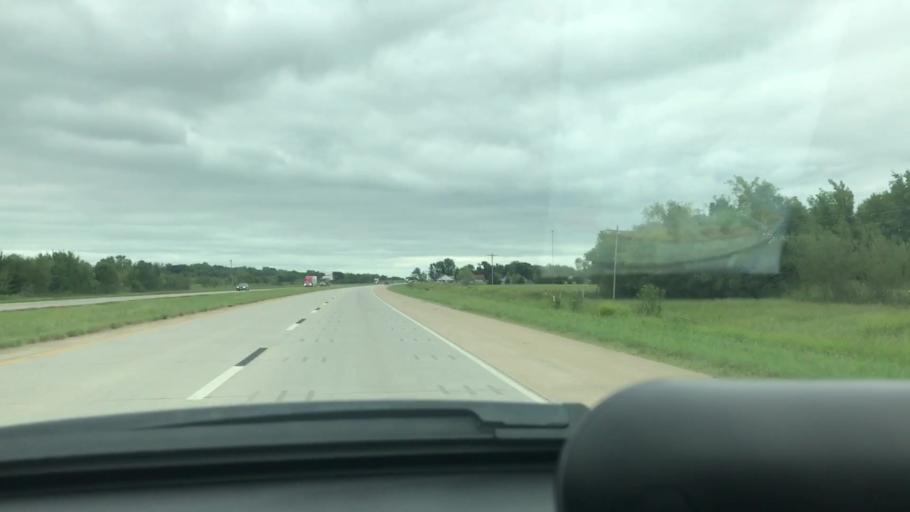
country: US
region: Oklahoma
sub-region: Mayes County
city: Chouteau
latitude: 36.0946
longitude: -95.3632
